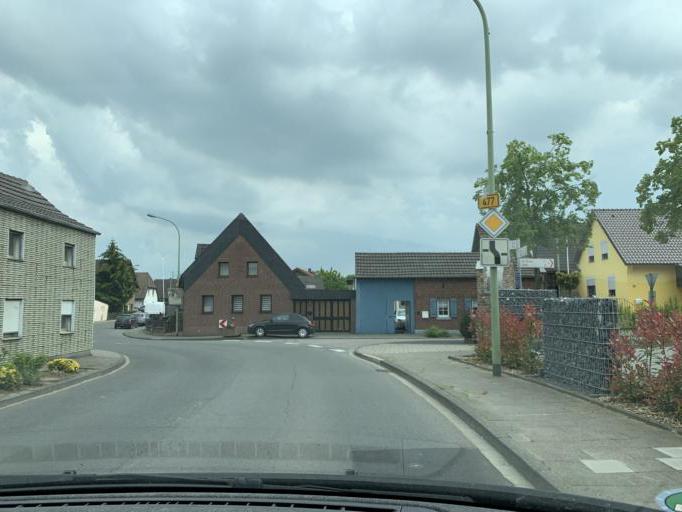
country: DE
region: North Rhine-Westphalia
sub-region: Regierungsbezirk Koln
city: Norvenich
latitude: 50.7728
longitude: 6.6329
